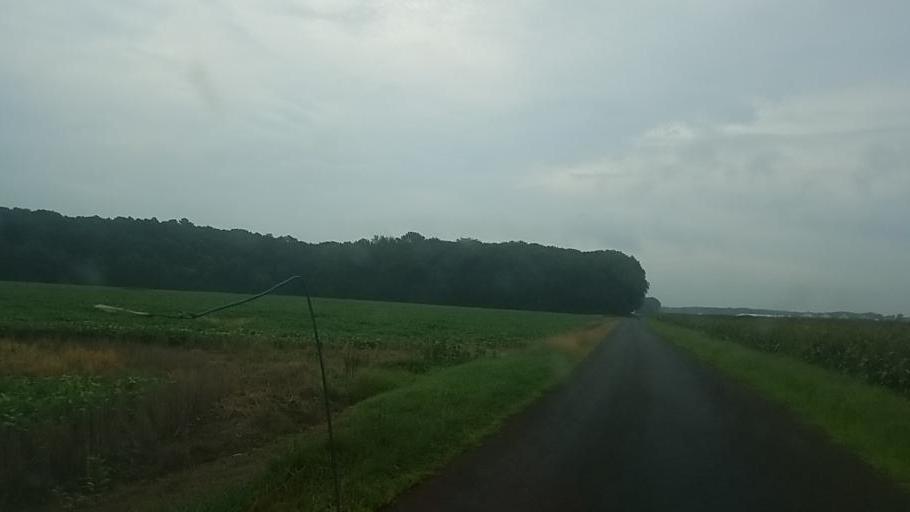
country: US
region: Delaware
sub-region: Sussex County
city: Selbyville
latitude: 38.4456
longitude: -75.2739
